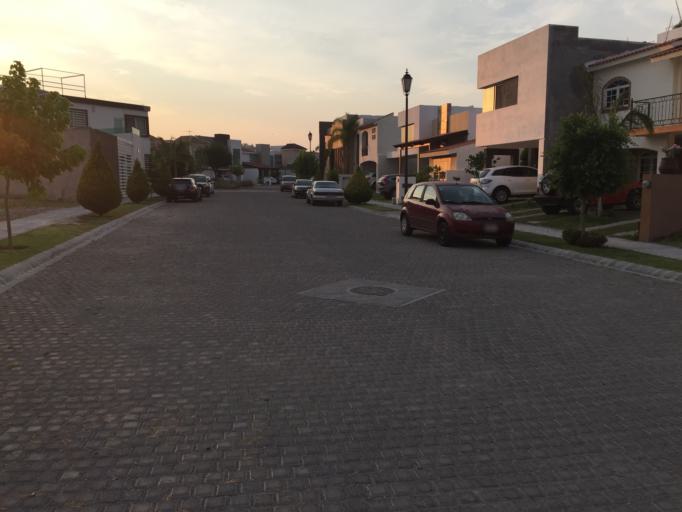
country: MX
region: Aguascalientes
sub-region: Aguascalientes
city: La Loma de los Negritos
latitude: 21.8455
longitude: -102.3554
